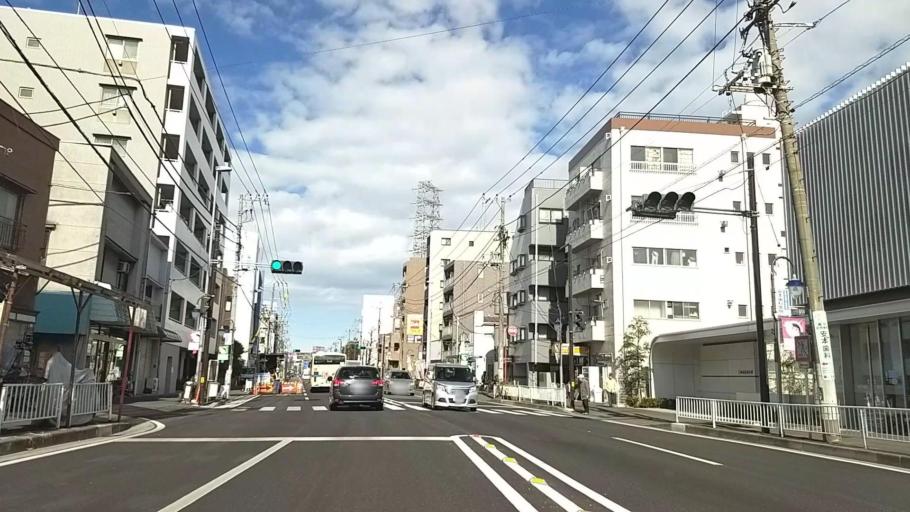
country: JP
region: Kanagawa
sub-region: Kawasaki-shi
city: Kawasaki
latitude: 35.5151
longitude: 139.6742
